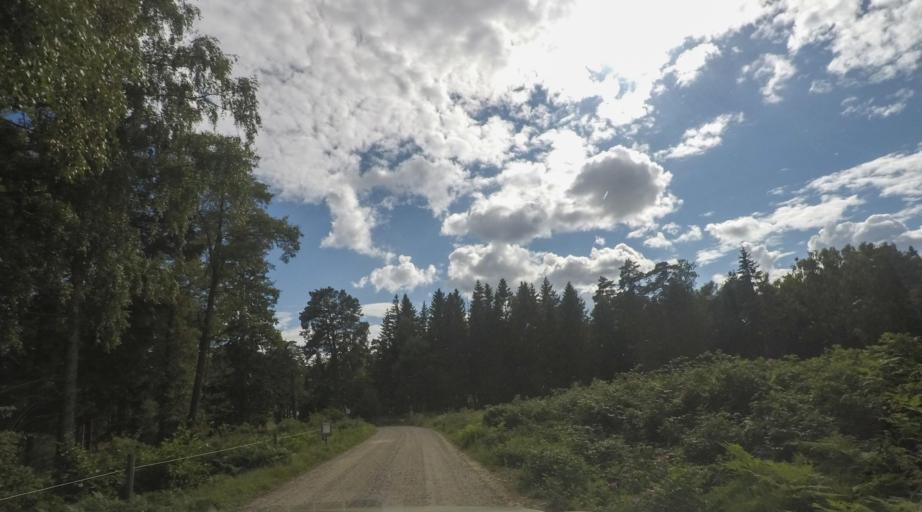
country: SE
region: Stockholm
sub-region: Sodertalje Kommun
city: Pershagen
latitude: 59.1055
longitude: 17.6785
